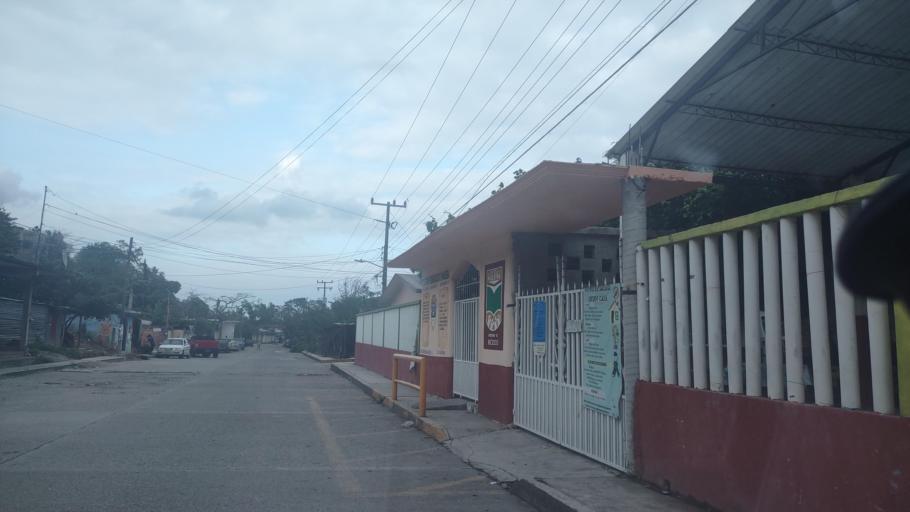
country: MX
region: Veracruz
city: Papantla de Olarte
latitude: 20.4517
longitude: -97.3126
